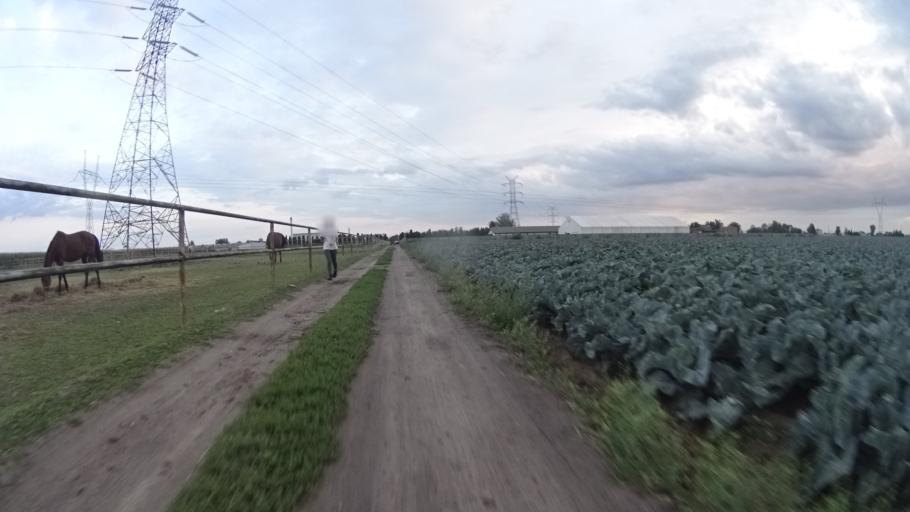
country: PL
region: Masovian Voivodeship
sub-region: Powiat warszawski zachodni
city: Ozarow Mazowiecki
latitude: 52.2381
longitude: 20.7659
